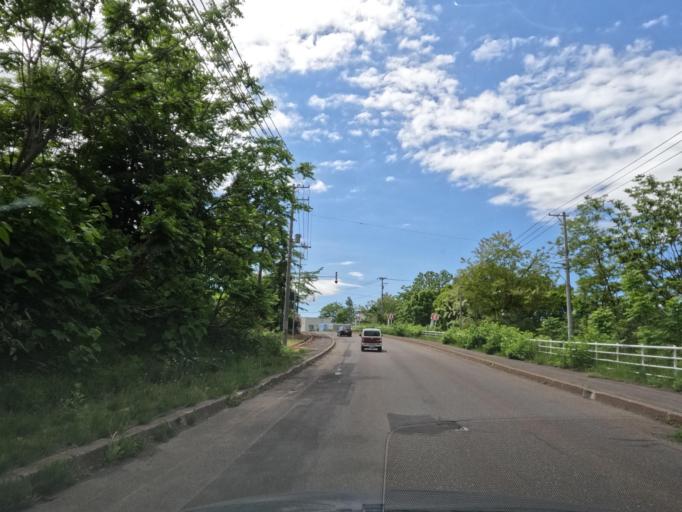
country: JP
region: Hokkaido
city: Bibai
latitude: 43.2536
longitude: 141.9187
